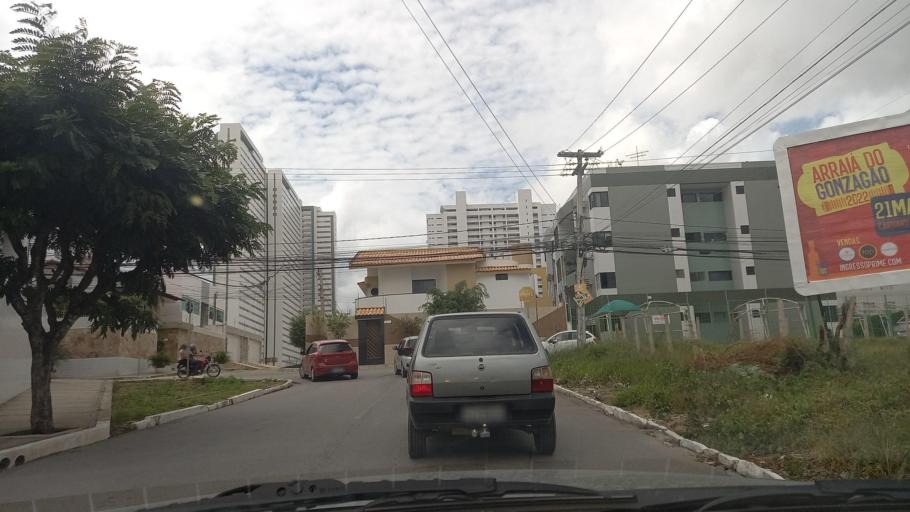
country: BR
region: Pernambuco
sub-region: Caruaru
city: Caruaru
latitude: -8.2659
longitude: -35.9665
